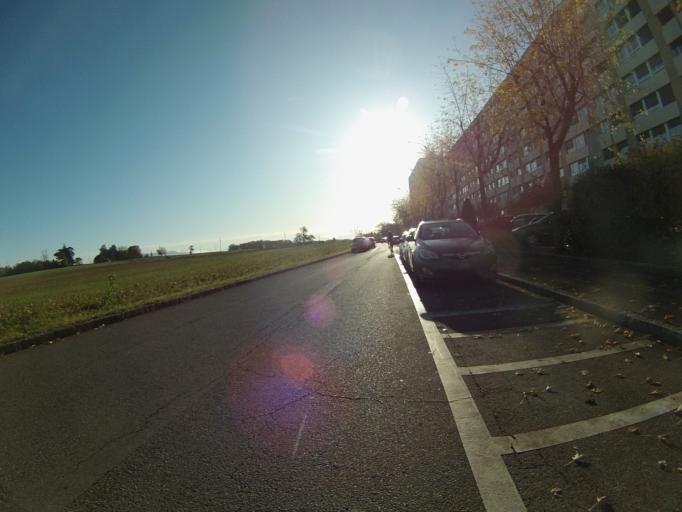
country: CH
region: Geneva
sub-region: Geneva
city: Meyrin
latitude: 46.2388
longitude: 6.0812
